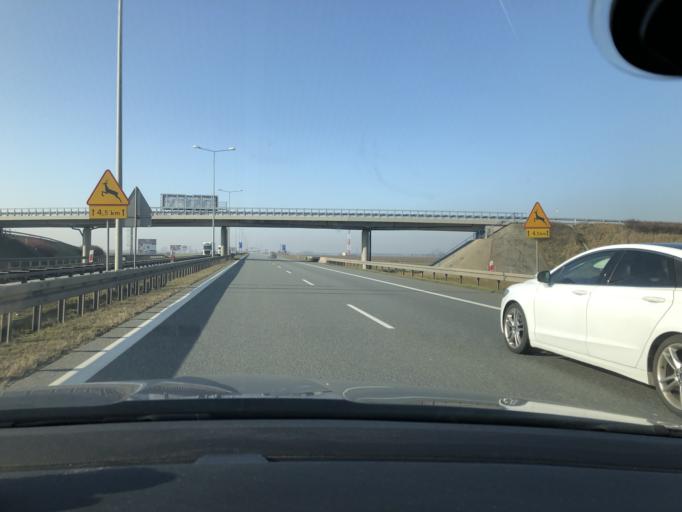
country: PL
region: Greater Poland Voivodeship
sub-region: Powiat poznanski
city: Komorniki
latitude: 52.3505
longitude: 16.7502
